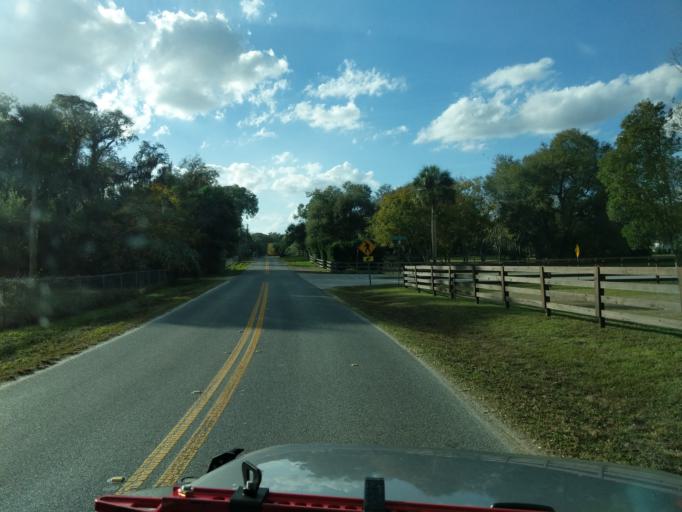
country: US
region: Florida
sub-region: Seminole County
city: Geneva
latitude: 28.7472
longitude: -81.1157
